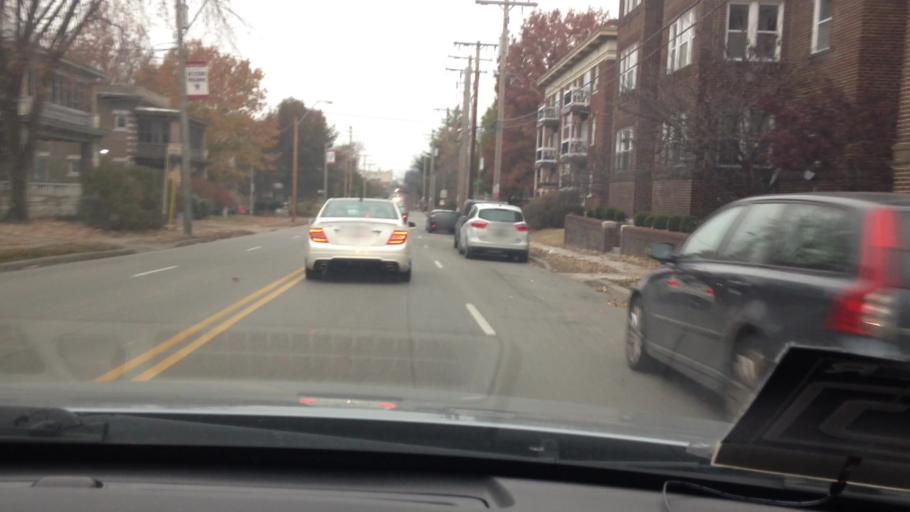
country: US
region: Missouri
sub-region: Jackson County
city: Kansas City
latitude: 39.0561
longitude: -94.5734
